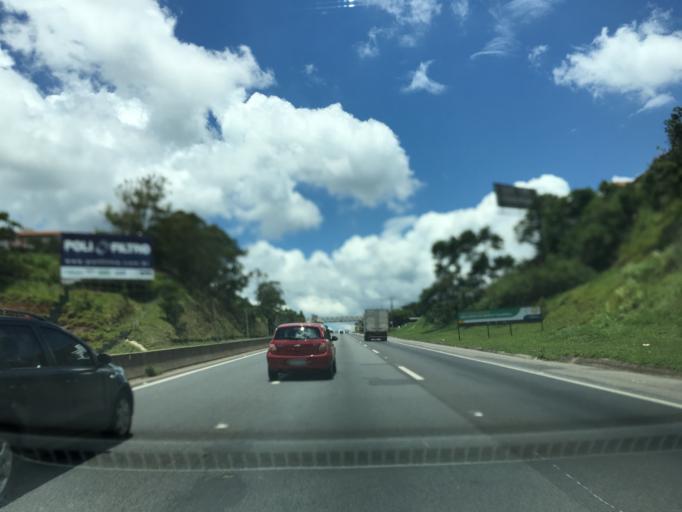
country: BR
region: Sao Paulo
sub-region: Mairipora
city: Mairipora
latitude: -23.2562
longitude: -46.5926
